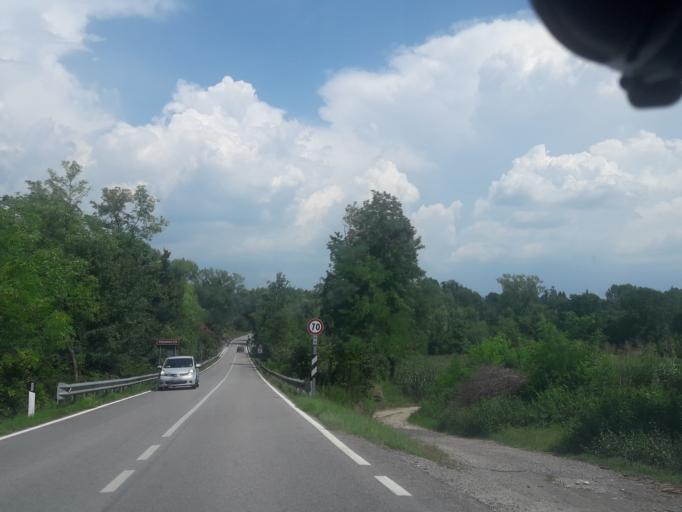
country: IT
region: Friuli Venezia Giulia
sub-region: Provincia di Udine
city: Reana del Roiale
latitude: 46.1281
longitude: 13.2023
